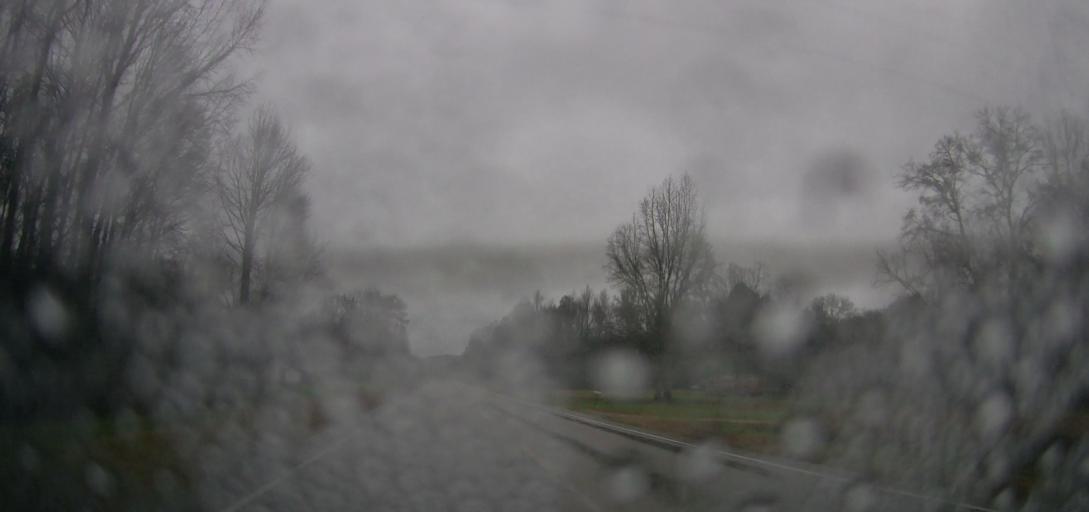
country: US
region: Alabama
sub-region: Autauga County
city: Prattville
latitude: 32.5084
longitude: -86.5870
